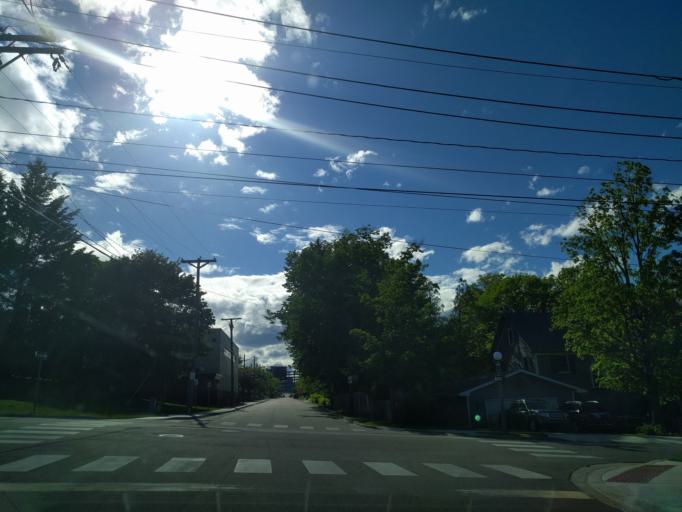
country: US
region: Michigan
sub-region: Marquette County
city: Marquette
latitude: 46.5422
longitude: -87.3977
